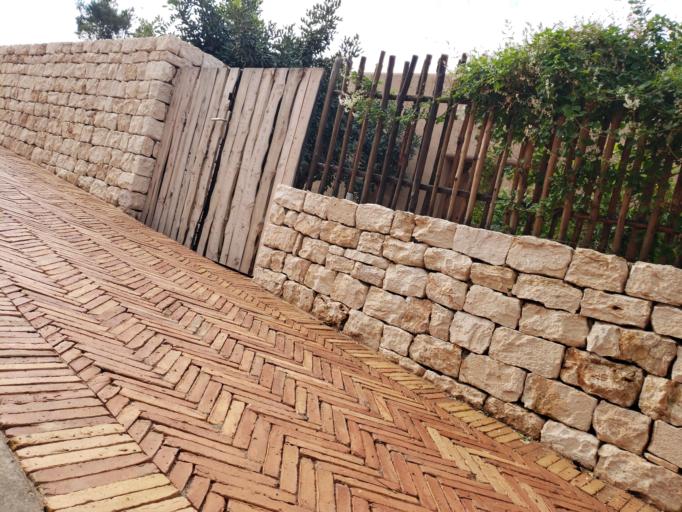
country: ES
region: Balearic Islands
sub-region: Illes Balears
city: Sant Joan de Labritja
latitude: 39.1104
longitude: 1.5089
